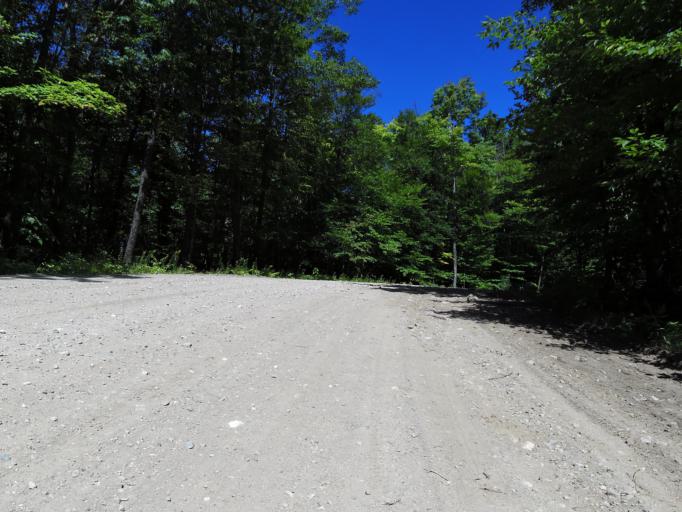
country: CA
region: Quebec
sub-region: Outaouais
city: Maniwaki
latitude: 46.2205
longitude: -76.1021
